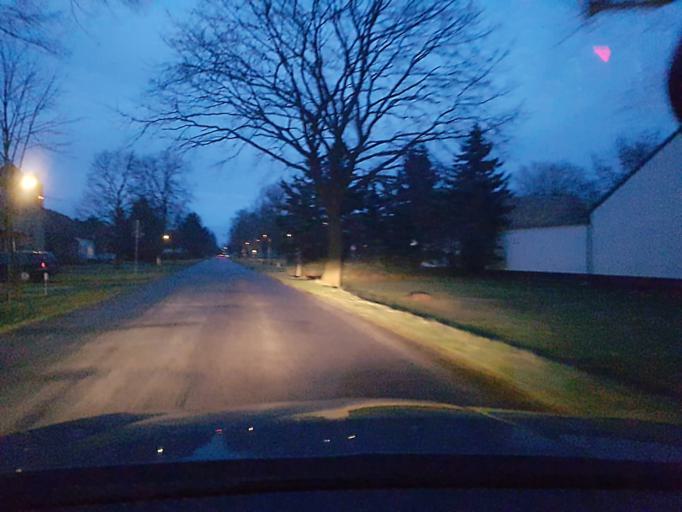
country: DE
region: Brandenburg
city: Ruckersdorf
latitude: 51.5898
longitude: 13.5350
